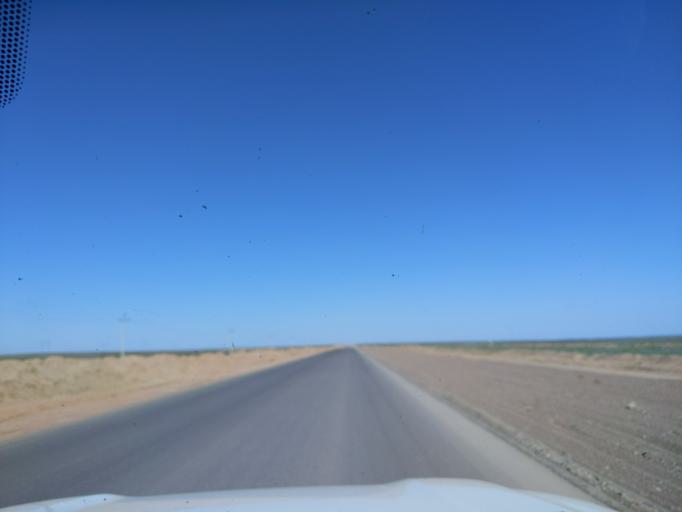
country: KZ
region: Almaty Oblysy
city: Bakanas
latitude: 44.1422
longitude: 75.8809
